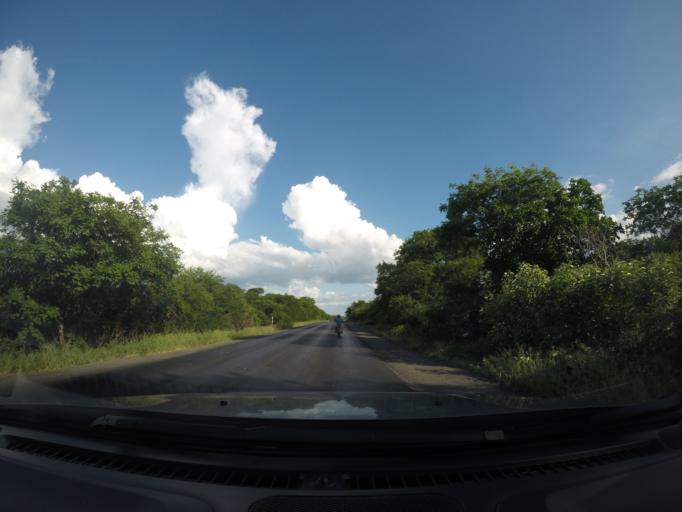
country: BR
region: Bahia
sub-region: Oliveira Dos Brejinhos
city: Oliveira dos Brejinhos
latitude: -12.0897
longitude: -42.9317
